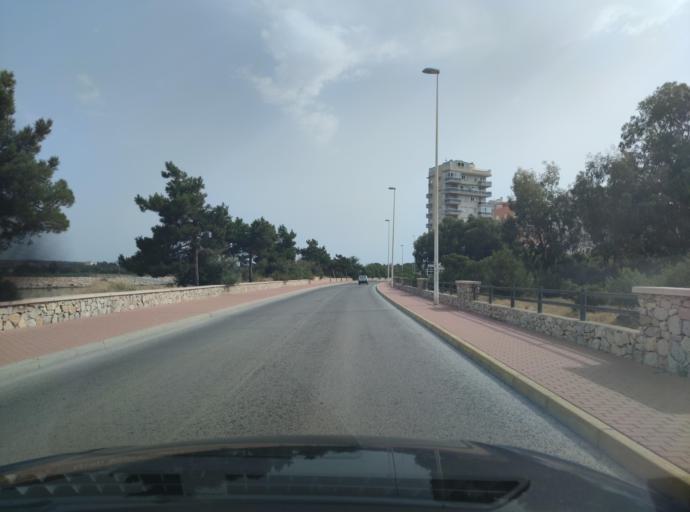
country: ES
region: Valencia
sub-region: Provincia de Alicante
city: Guardamar del Segura
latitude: 38.1074
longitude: -0.6533
